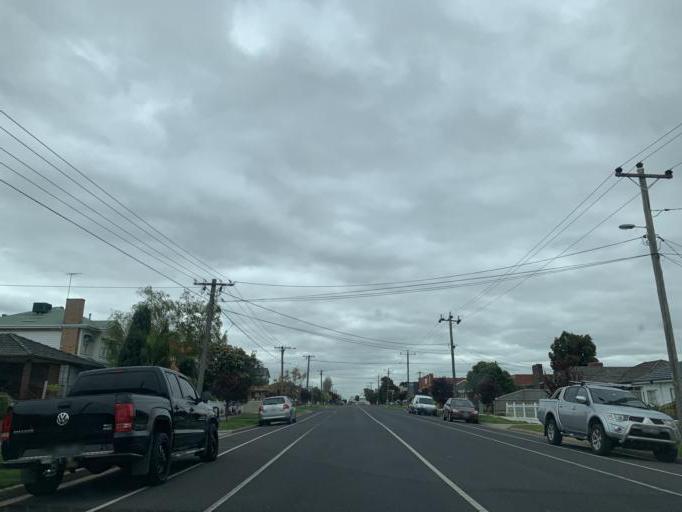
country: AU
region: Victoria
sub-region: Moreland
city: Pascoe Vale South
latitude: -37.7305
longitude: 144.9461
